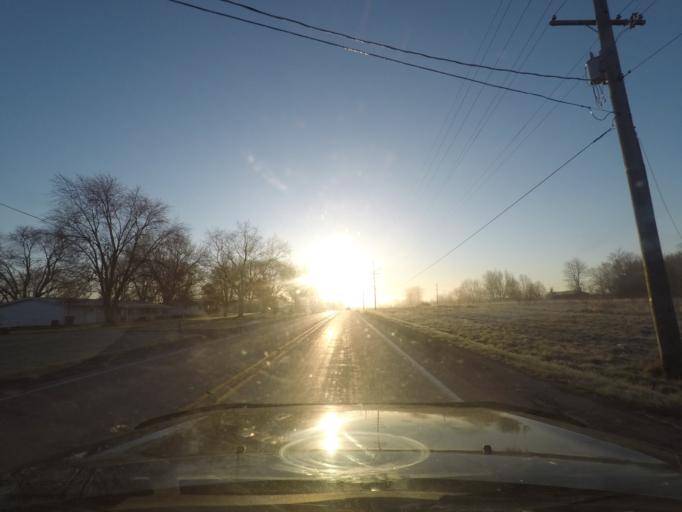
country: US
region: Indiana
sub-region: Marshall County
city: Bremen
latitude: 41.4542
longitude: -86.1252
